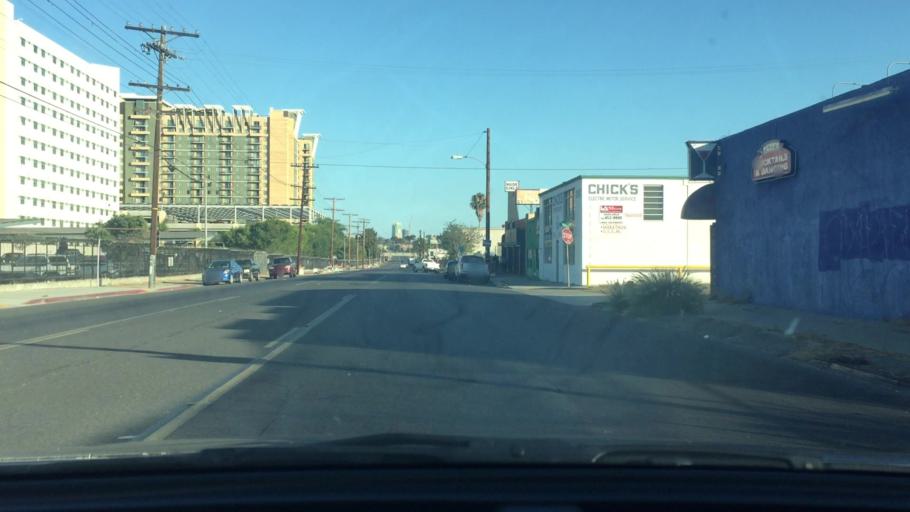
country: US
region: California
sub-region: San Diego County
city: National City
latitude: 32.6865
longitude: -117.1168
